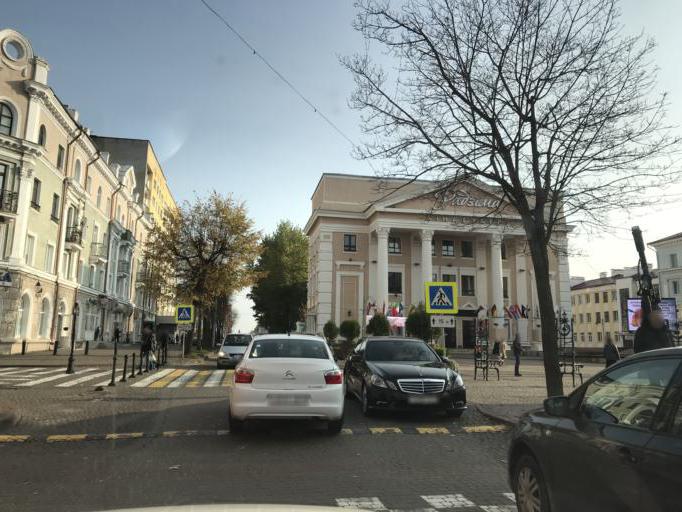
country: BY
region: Mogilev
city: Mahilyow
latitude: 53.9027
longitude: 30.3406
